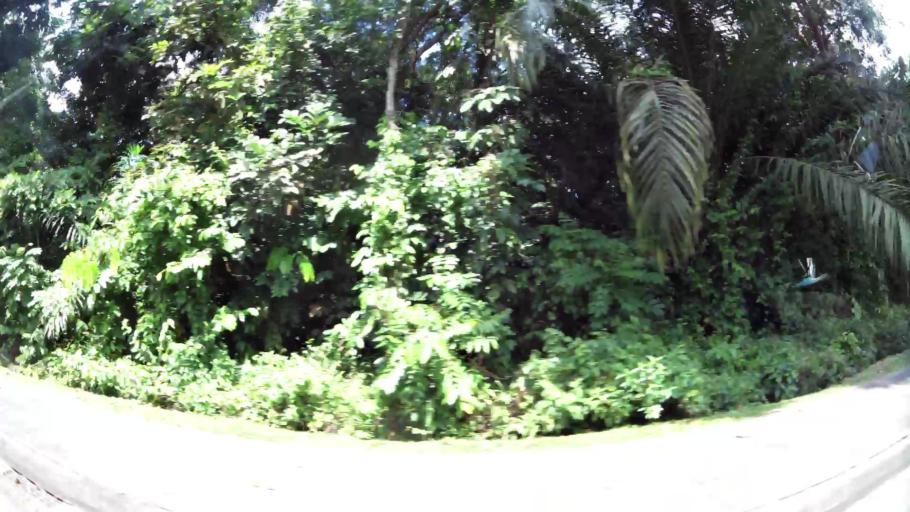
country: SG
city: Singapore
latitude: 1.3383
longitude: 103.8018
